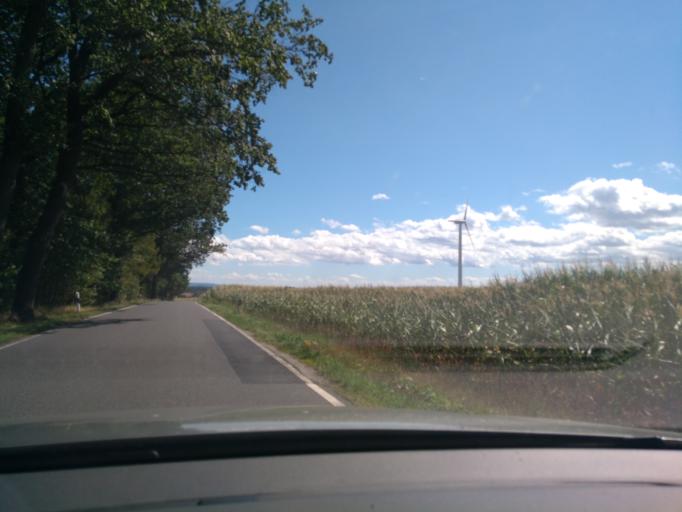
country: DE
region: Saxony
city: Arnsdorf
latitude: 51.1363
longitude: 13.9586
